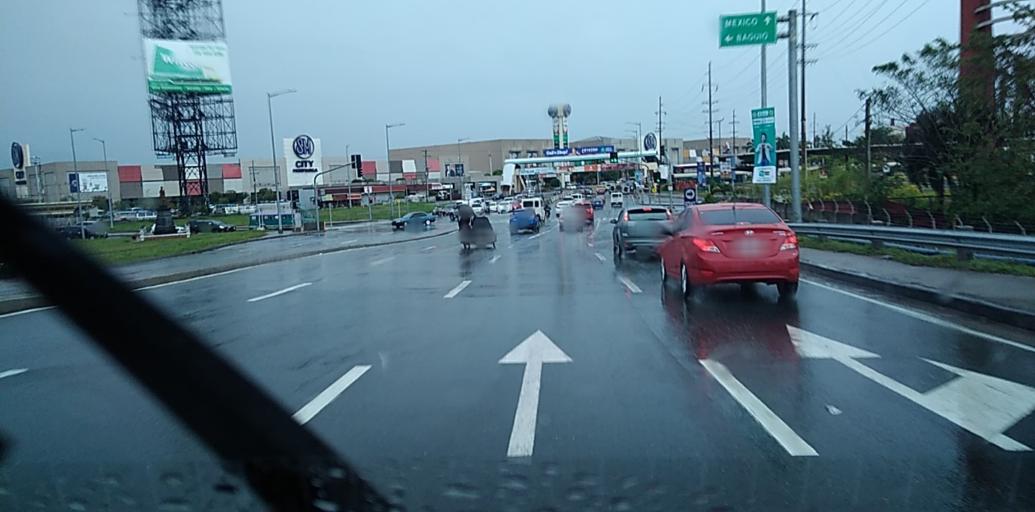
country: PH
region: Central Luzon
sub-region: Province of Pampanga
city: Del Pilar
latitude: 15.0499
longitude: 120.6958
